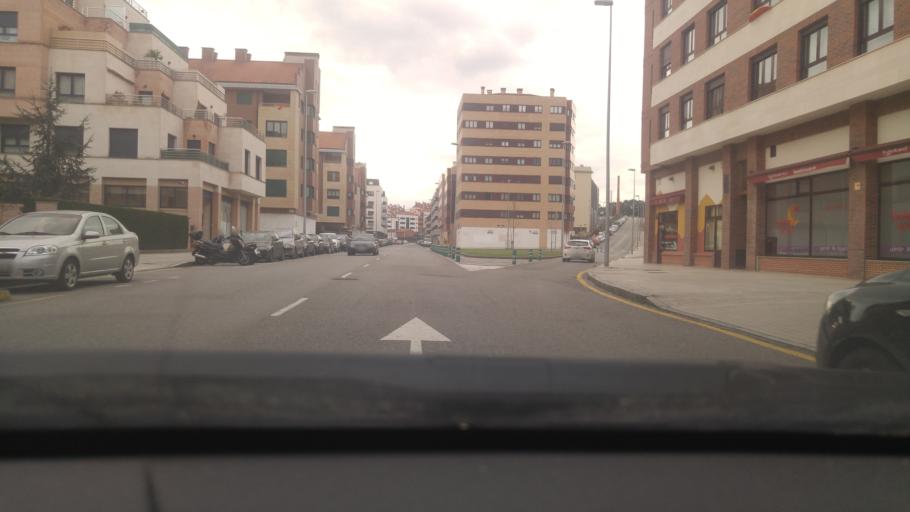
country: ES
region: Asturias
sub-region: Province of Asturias
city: Gijon
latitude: 43.5251
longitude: -5.6511
